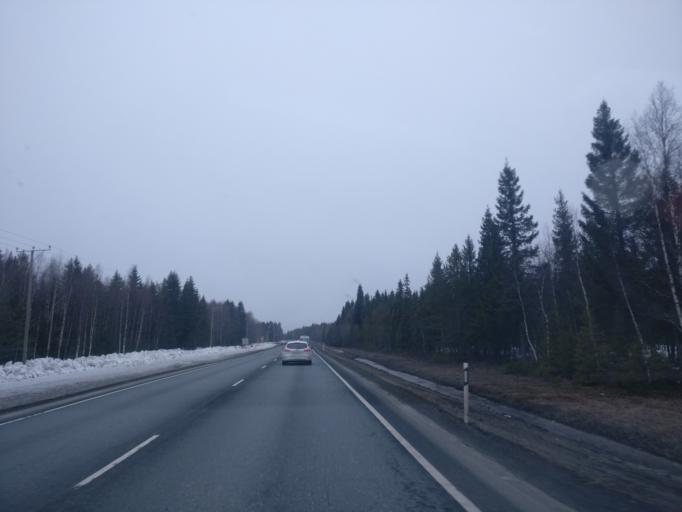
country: FI
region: Lapland
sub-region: Kemi-Tornio
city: Simo
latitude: 65.6723
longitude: 24.9112
